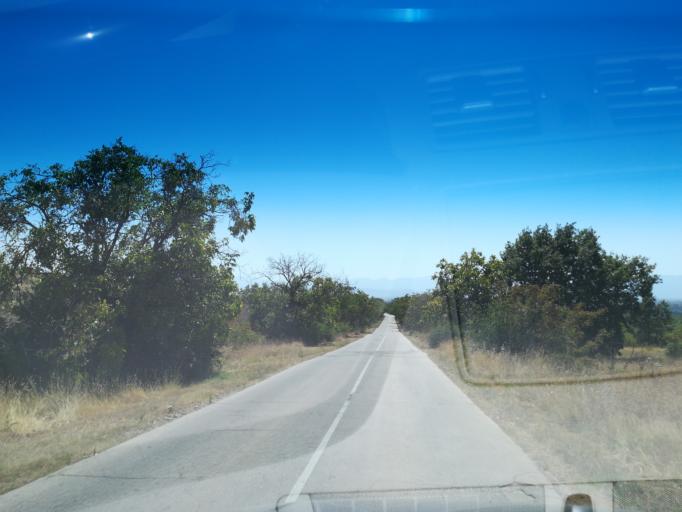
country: BG
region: Pazardzhik
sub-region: Obshtina Pazardzhik
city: Pazardzhik
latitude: 42.3084
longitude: 24.3986
